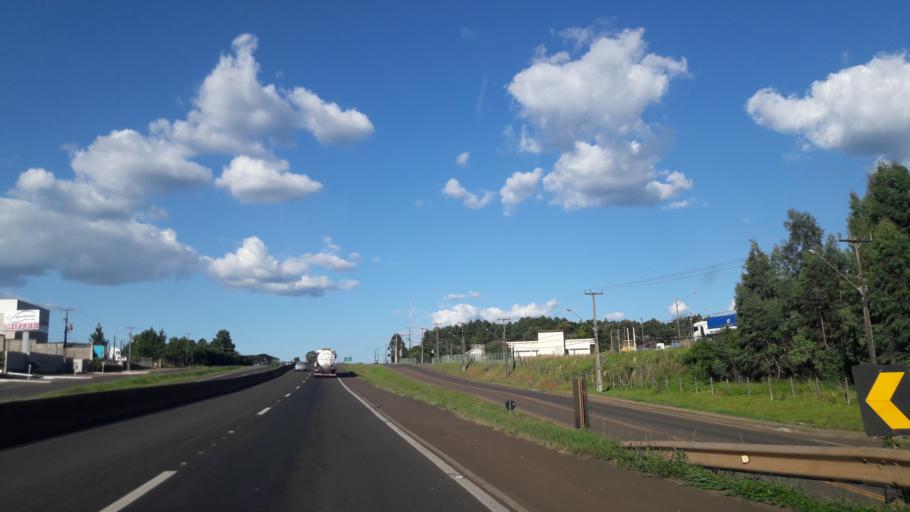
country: BR
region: Parana
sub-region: Guarapuava
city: Guarapuava
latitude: -25.3522
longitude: -51.4585
